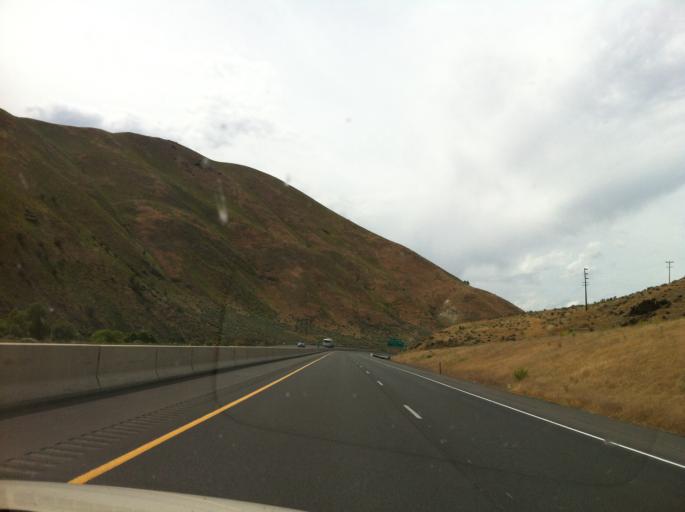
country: US
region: Idaho
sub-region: Washington County
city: Weiser
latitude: 44.4152
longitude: -117.3078
